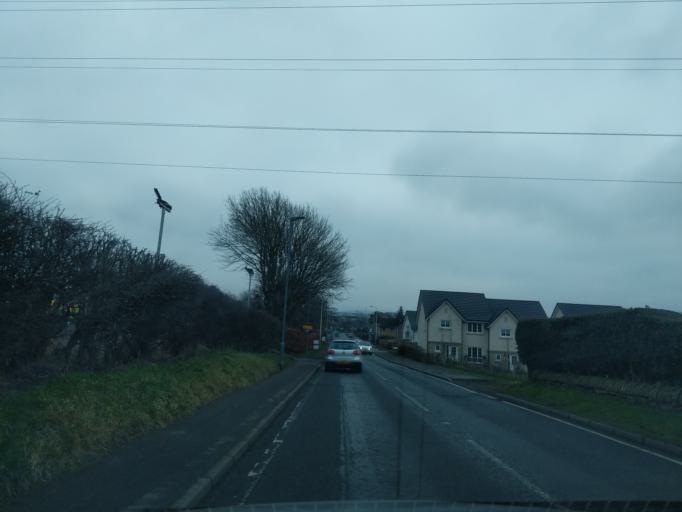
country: GB
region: Scotland
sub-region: Edinburgh
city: Currie
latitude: 55.9022
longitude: -3.3105
